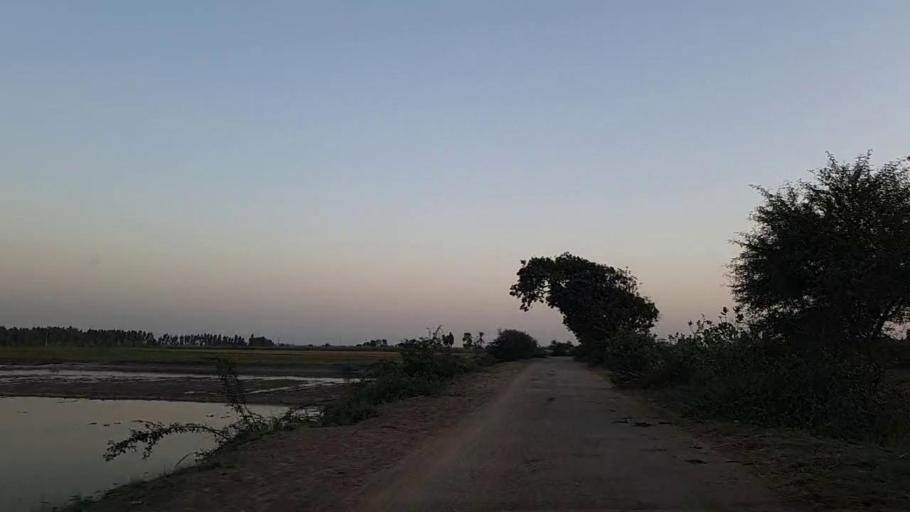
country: PK
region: Sindh
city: Mirpur Batoro
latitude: 24.6162
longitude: 68.1844
